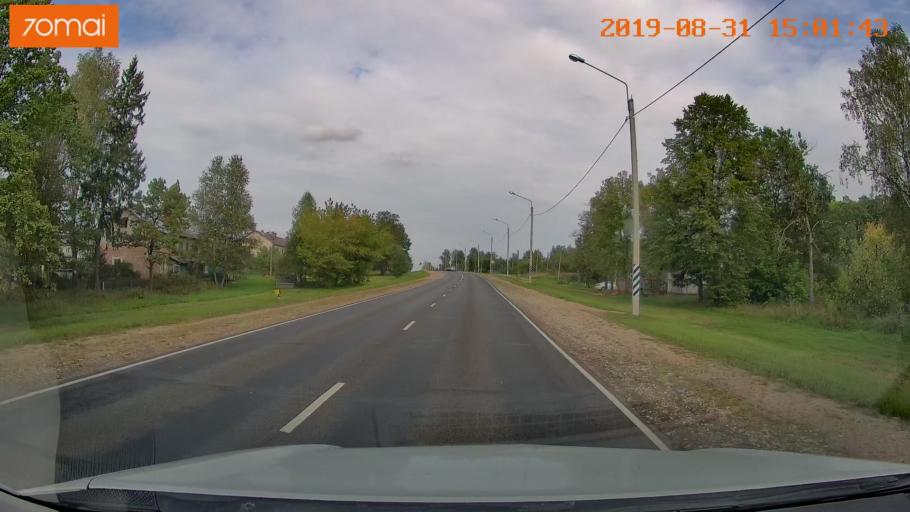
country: RU
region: Kaluga
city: Spas-Demensk
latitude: 54.3411
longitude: 34.0626
